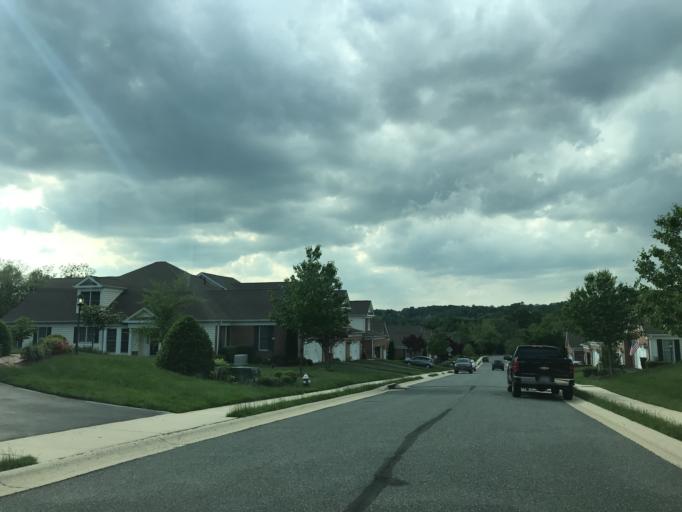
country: US
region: Maryland
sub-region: Harford County
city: North Bel Air
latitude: 39.5207
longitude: -76.3674
